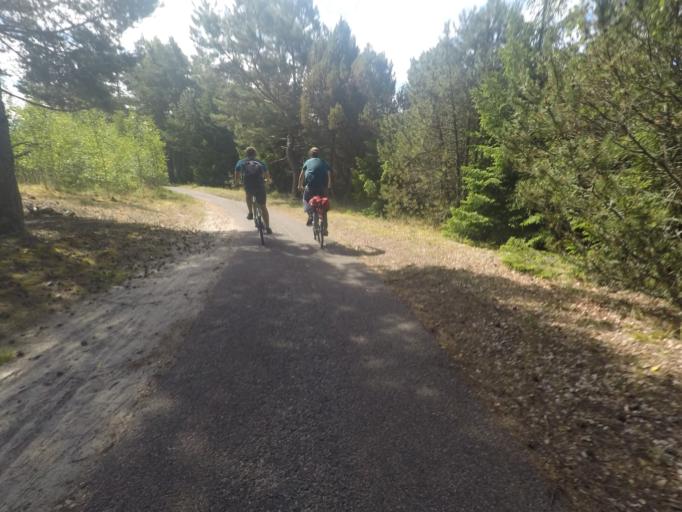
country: LT
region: Klaipedos apskritis
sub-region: Klaipeda
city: Klaipeda
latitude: 55.6047
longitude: 21.1179
